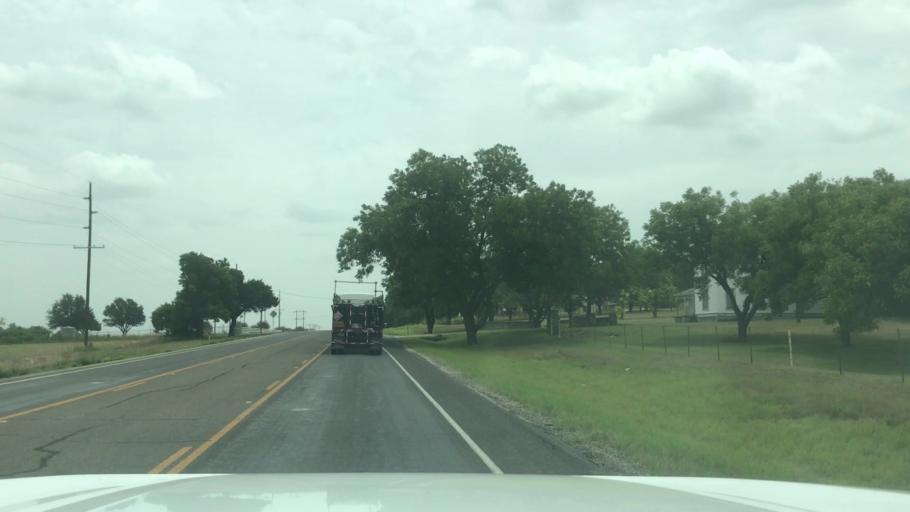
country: US
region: Texas
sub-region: Bosque County
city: Clifton
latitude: 31.7701
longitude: -97.5697
